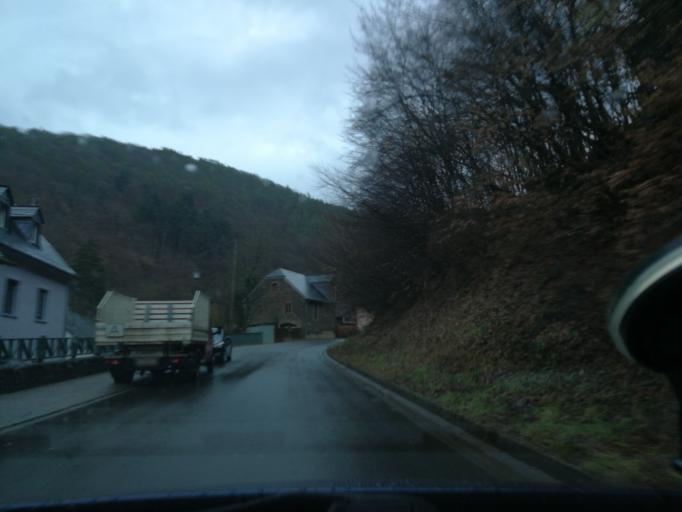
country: DE
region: Rheinland-Pfalz
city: Heidenburg
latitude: 49.8264
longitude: 6.9441
